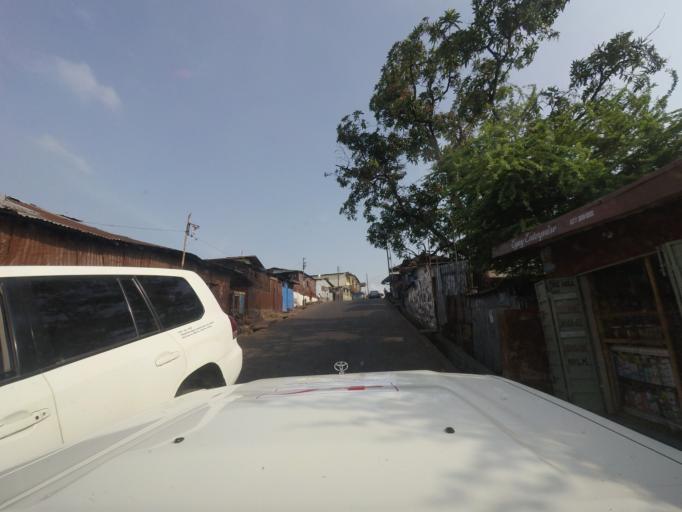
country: SL
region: Western Area
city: Freetown
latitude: 8.4850
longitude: -13.2412
